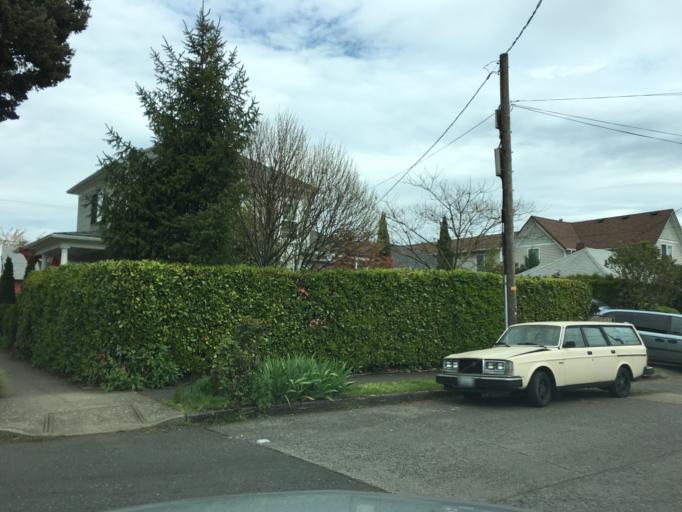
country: US
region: Oregon
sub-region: Multnomah County
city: Lents
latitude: 45.5255
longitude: -122.5815
